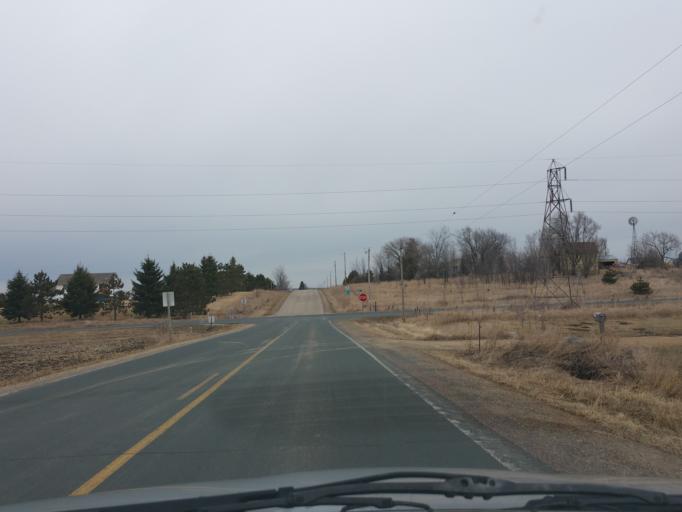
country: US
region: Wisconsin
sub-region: Saint Croix County
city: Roberts
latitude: 45.0347
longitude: -92.5578
